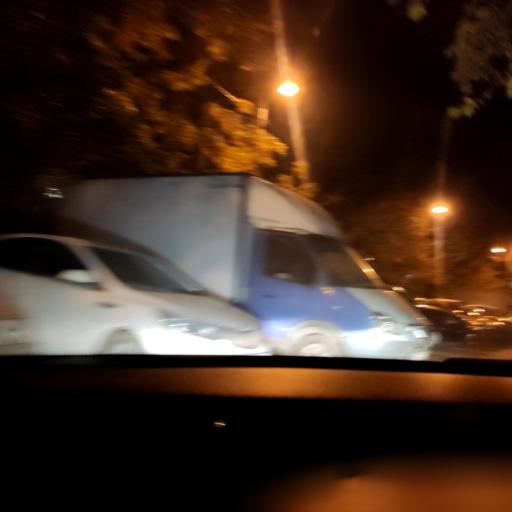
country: RU
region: Samara
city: Smyshlyayevka
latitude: 53.2188
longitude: 50.2715
